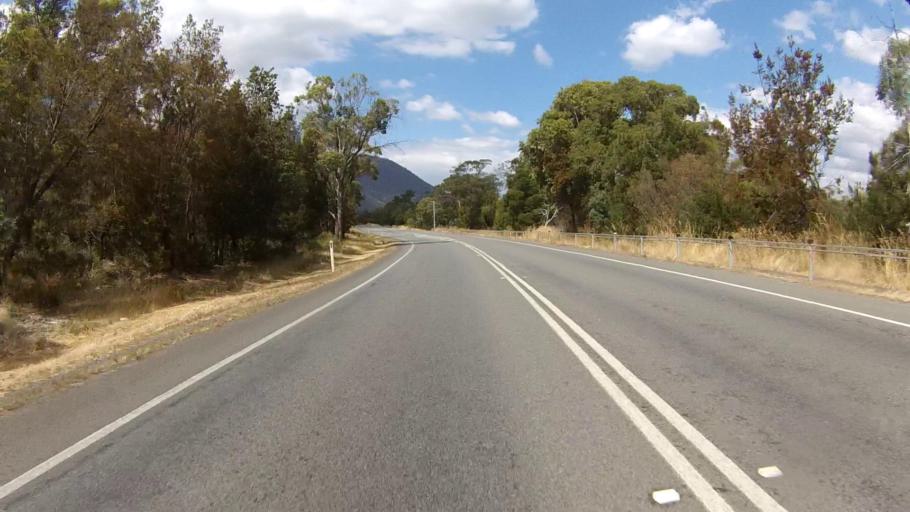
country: AU
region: Tasmania
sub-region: Brighton
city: Old Beach
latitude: -42.7763
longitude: 147.2704
